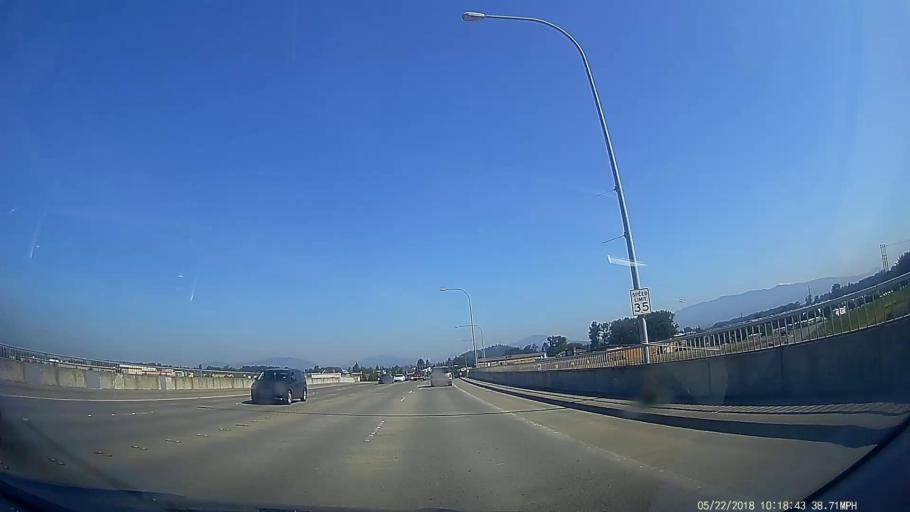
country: US
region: Washington
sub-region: Skagit County
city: Mount Vernon
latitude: 48.4452
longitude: -122.3355
